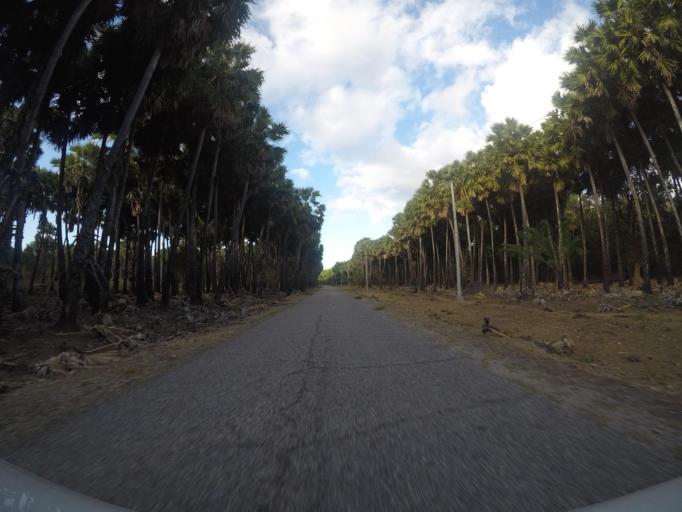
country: TL
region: Lautem
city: Lospalos
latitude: -8.3339
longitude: 126.9543
